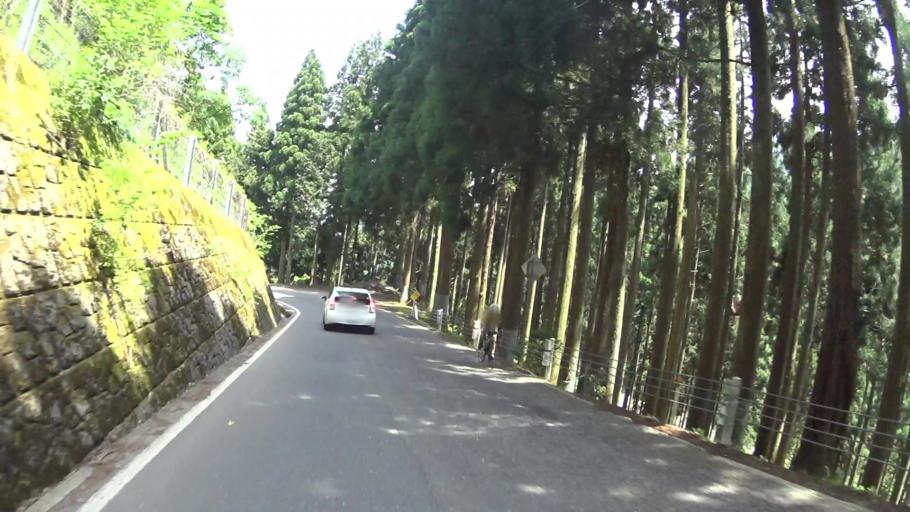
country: JP
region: Kyoto
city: Maizuru
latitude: 35.4438
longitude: 135.5018
